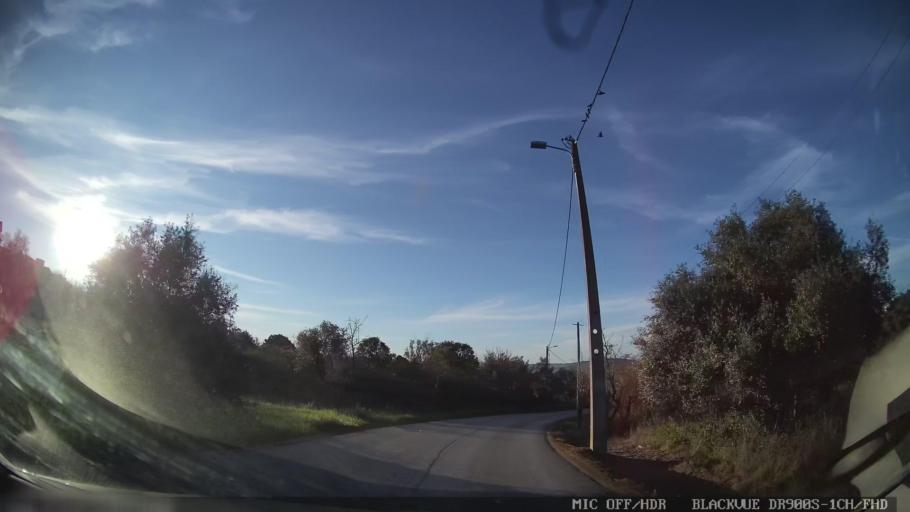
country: PT
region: Lisbon
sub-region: Vila Franca de Xira
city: Vila Franca de Xira
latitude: 38.9880
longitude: -9.0149
